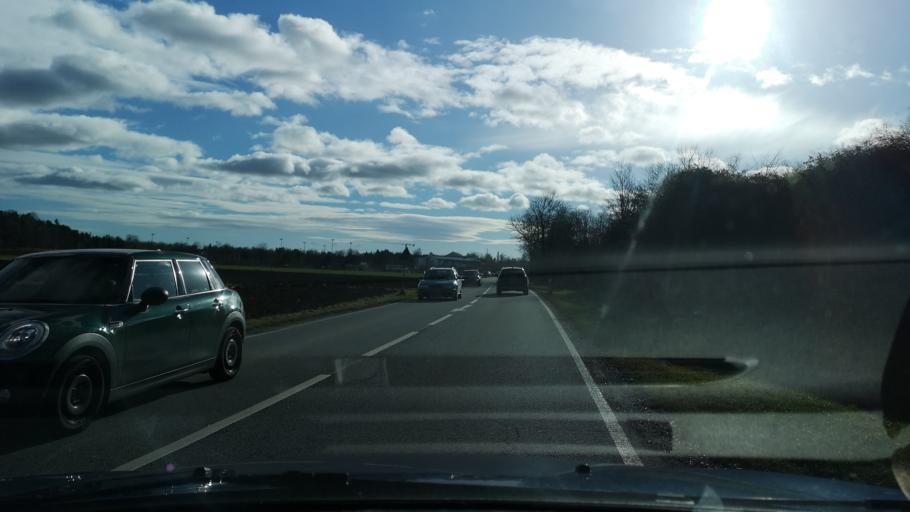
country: DE
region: Bavaria
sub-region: Upper Bavaria
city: Poing
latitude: 48.1802
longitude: 11.8090
